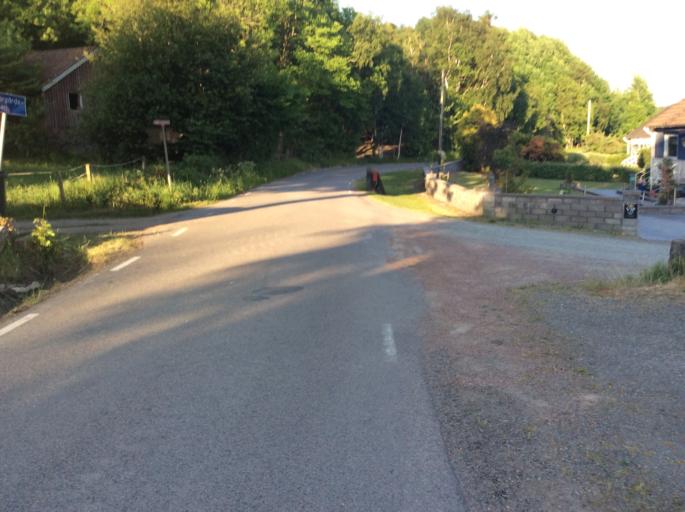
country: SE
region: Vaestra Goetaland
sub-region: Goteborg
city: Majorna
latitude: 57.7924
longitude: 11.8784
